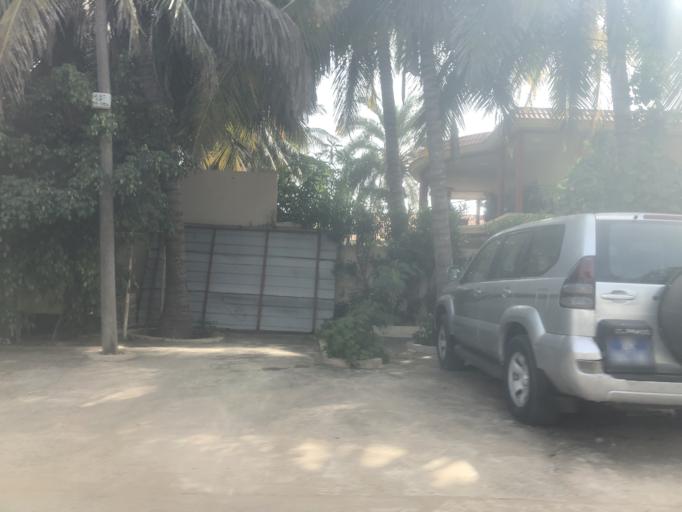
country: SN
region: Dakar
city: Mermoz Boabab
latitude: 14.7381
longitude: -17.5124
